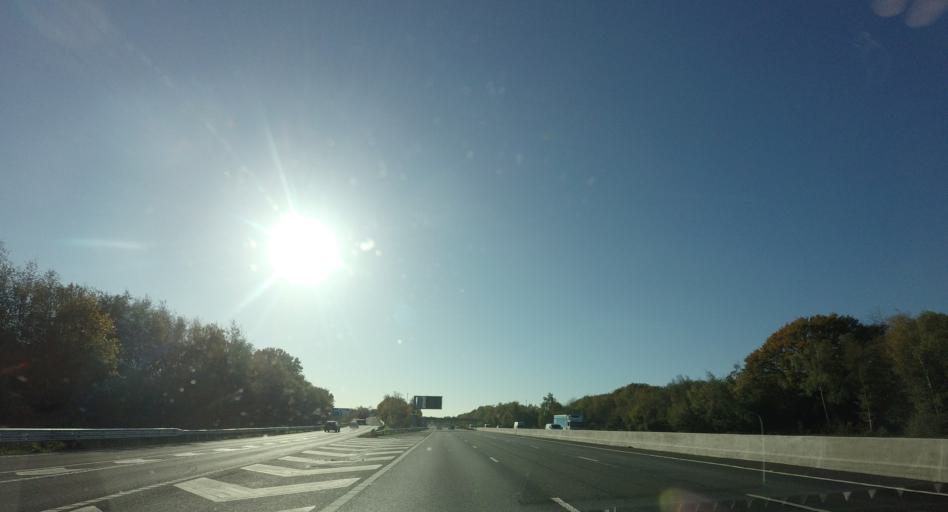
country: GB
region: England
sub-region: West Sussex
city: Copthorne
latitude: 51.1359
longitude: -0.1404
